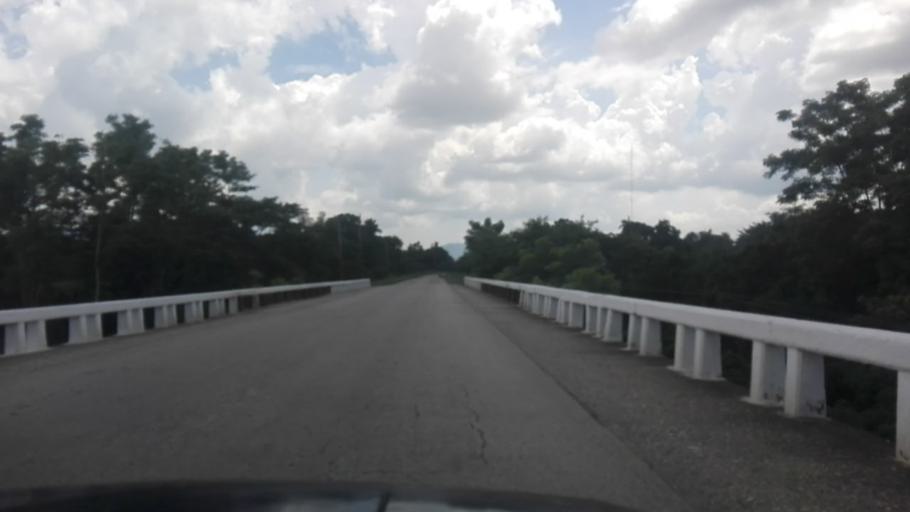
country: CU
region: Granma
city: Bartolome Maso
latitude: 20.1464
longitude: -76.9610
